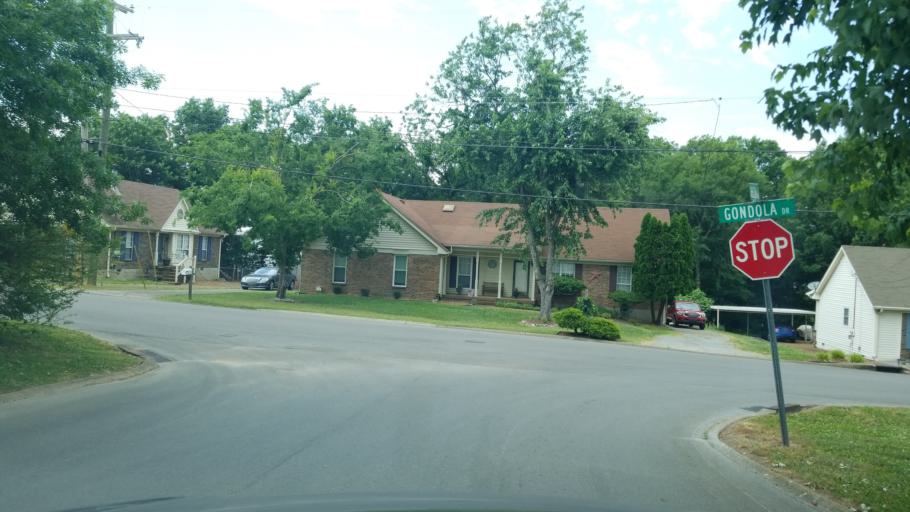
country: US
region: Tennessee
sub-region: Rutherford County
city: La Vergne
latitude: 36.0824
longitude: -86.6035
